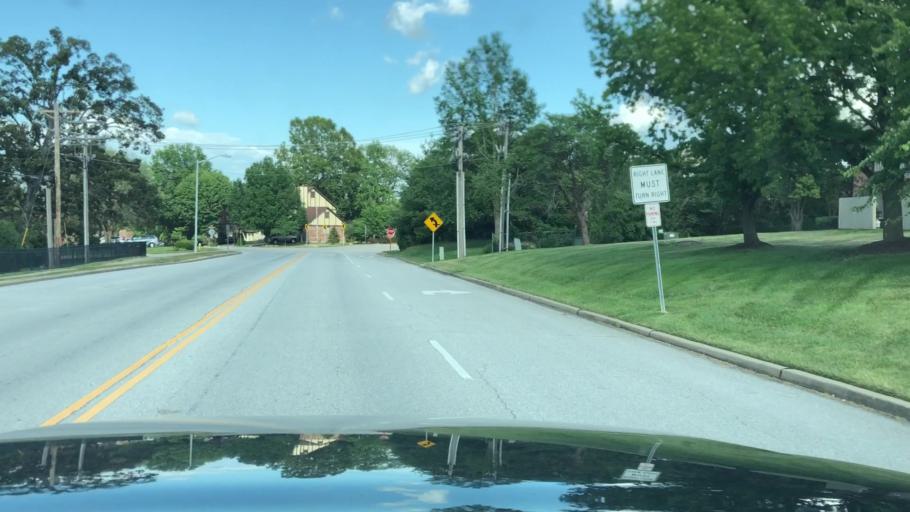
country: US
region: Missouri
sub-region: Saint Charles County
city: Lake Saint Louis
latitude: 38.7959
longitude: -90.8087
